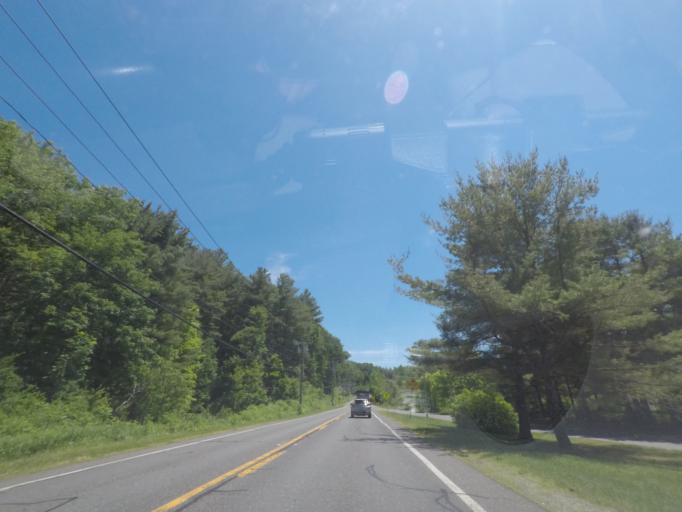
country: US
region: Massachusetts
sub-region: Berkshire County
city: Becket
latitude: 42.2928
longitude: -73.1605
